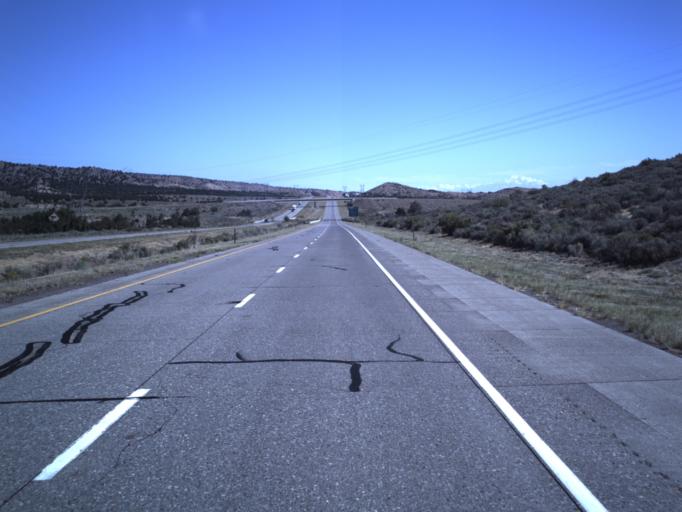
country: US
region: Utah
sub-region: Sevier County
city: Monroe
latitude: 38.5838
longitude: -112.2764
